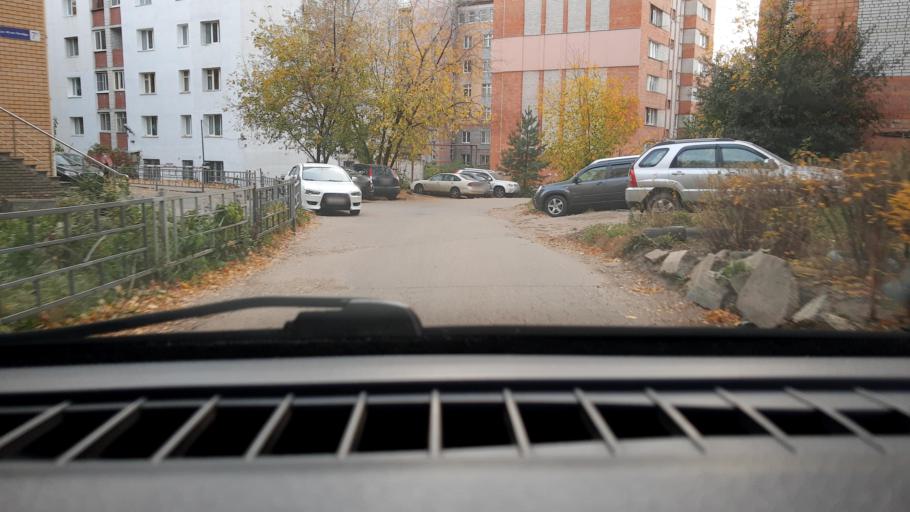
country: RU
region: Nizjnij Novgorod
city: Nizhniy Novgorod
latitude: 56.2599
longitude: 43.9814
